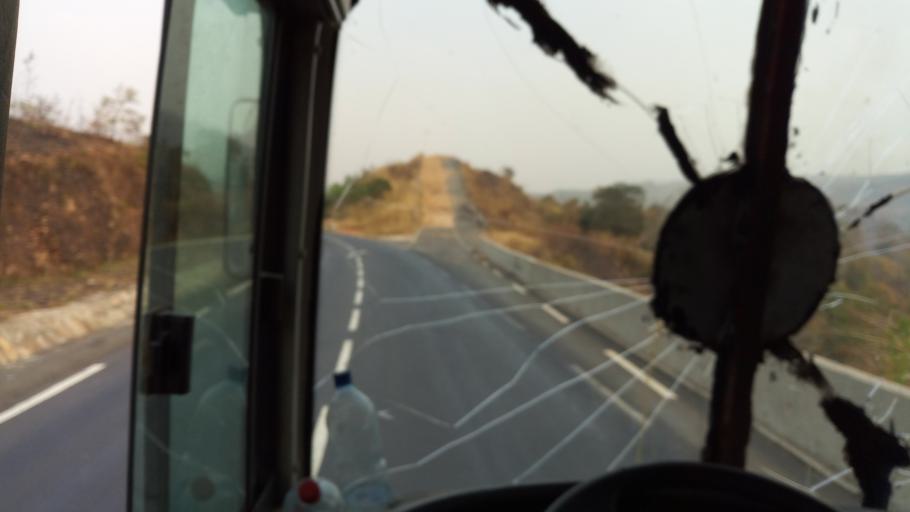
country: TG
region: Kara
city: Bafilo
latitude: 9.3480
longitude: 1.2696
